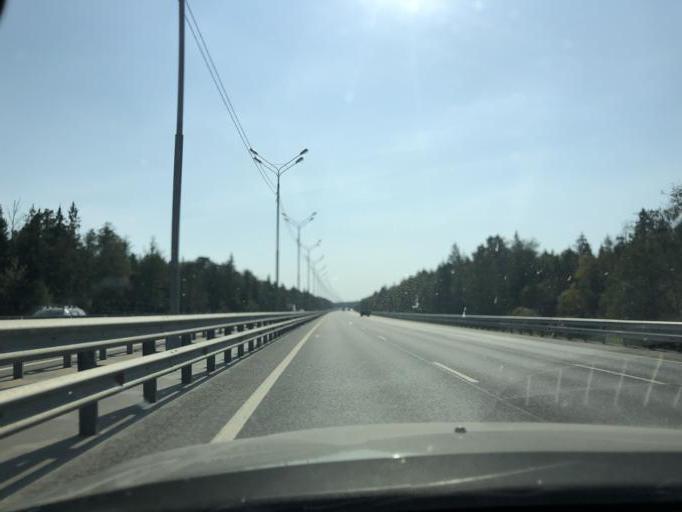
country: RU
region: Moskovskaya
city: Novyy Byt
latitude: 55.0062
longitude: 37.5502
